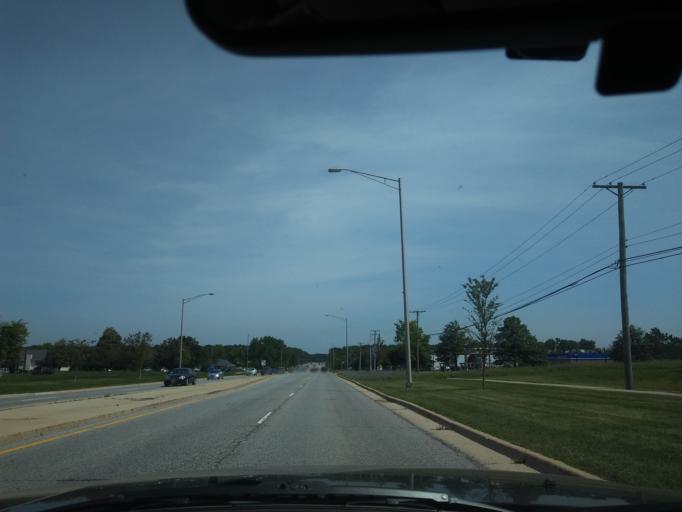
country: US
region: Illinois
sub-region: Cook County
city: Tinley Park
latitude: 41.6117
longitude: -87.7943
